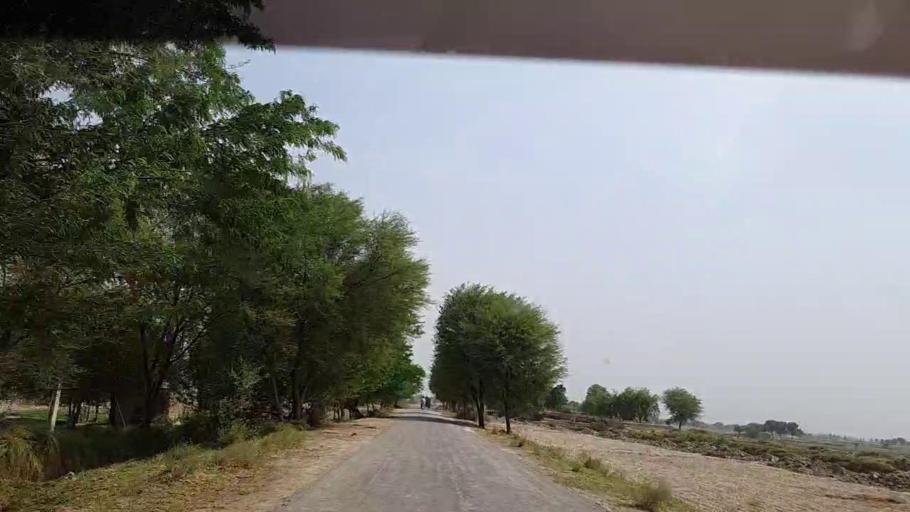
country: PK
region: Sindh
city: Khairpur Nathan Shah
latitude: 27.0720
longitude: 67.6878
